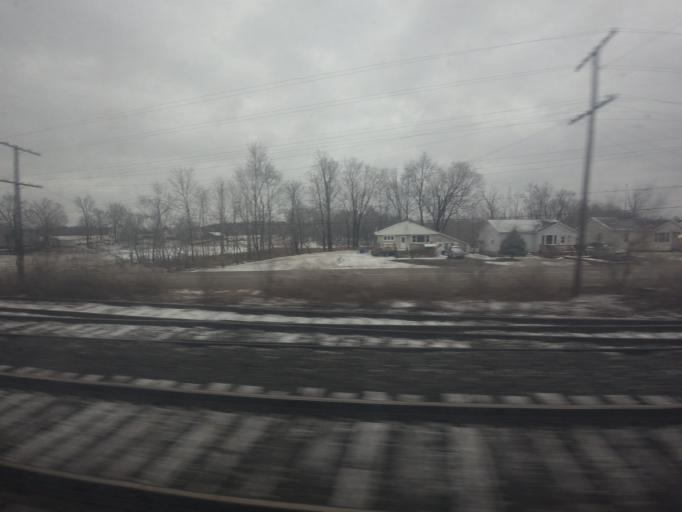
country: CA
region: Ontario
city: Gananoque
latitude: 44.3685
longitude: -76.1566
